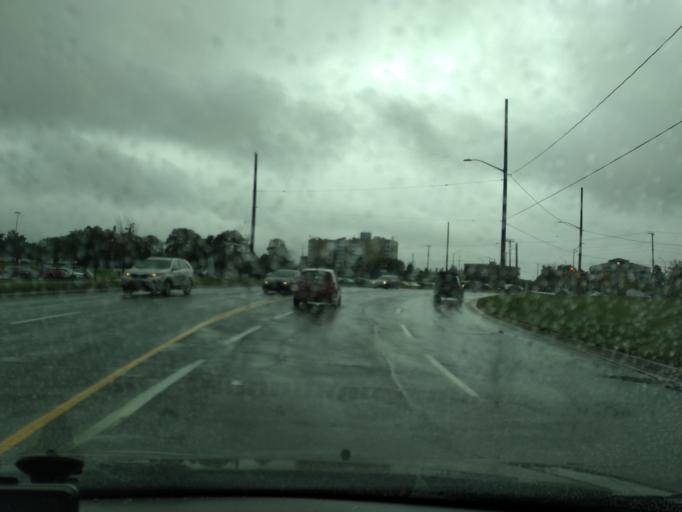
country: CA
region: Ontario
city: Barrie
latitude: 44.4126
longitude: -79.6716
